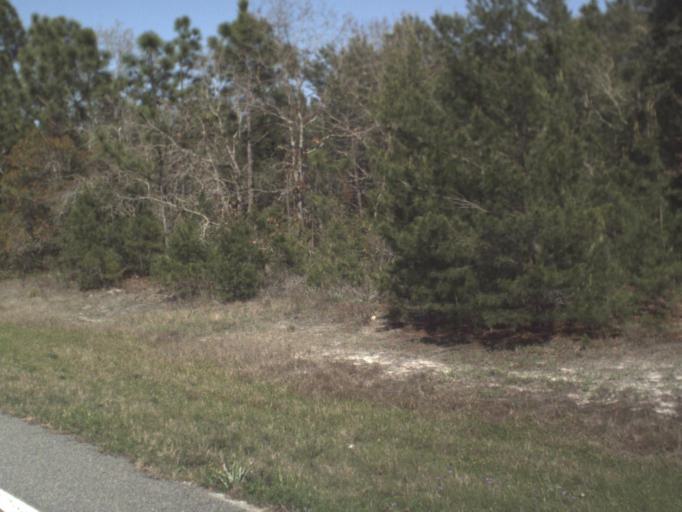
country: US
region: Florida
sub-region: Wakulla County
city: Crawfordville
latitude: 29.9563
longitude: -84.3851
